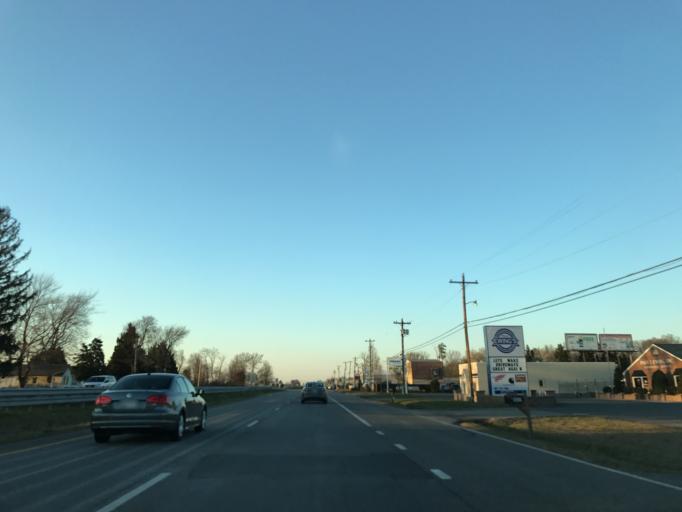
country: US
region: Maryland
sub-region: Talbot County
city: Easton
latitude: 38.8057
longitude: -76.0600
